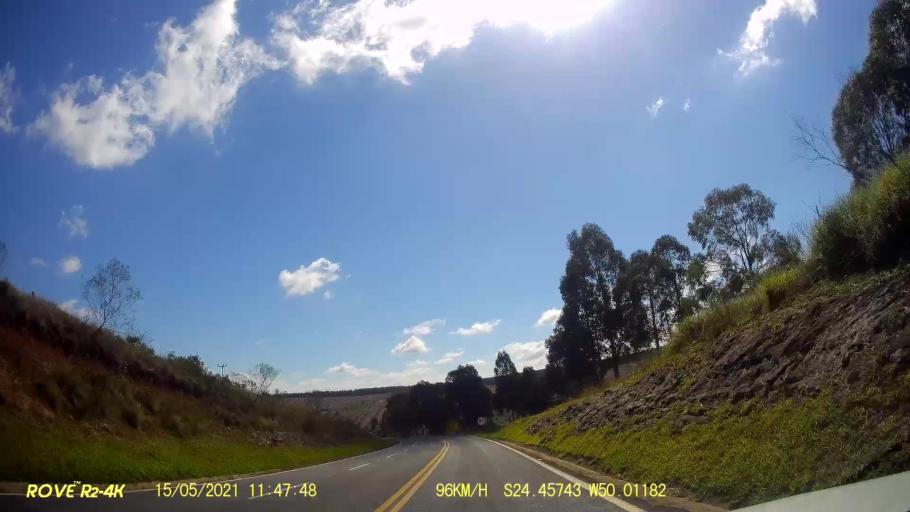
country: BR
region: Parana
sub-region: Pirai Do Sul
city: Pirai do Sul
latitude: -24.4577
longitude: -50.0117
